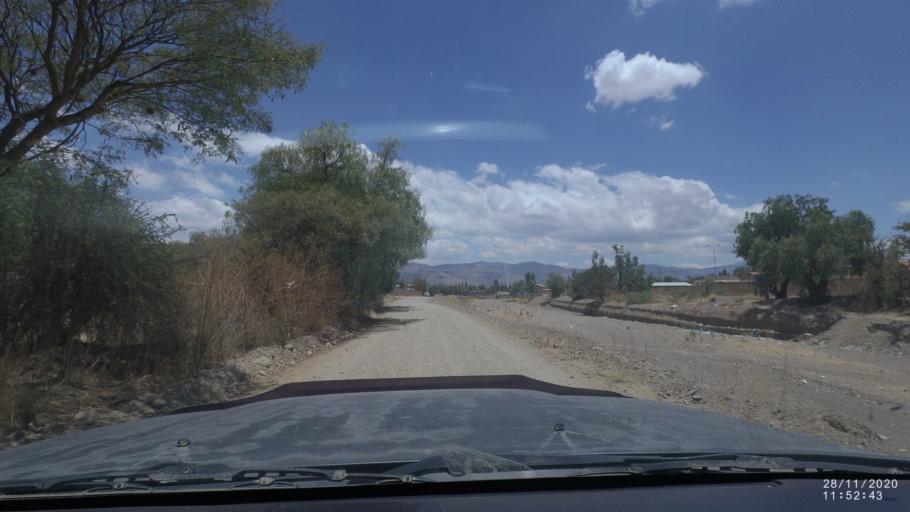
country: BO
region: Cochabamba
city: Tarata
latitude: -17.6144
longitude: -66.0216
